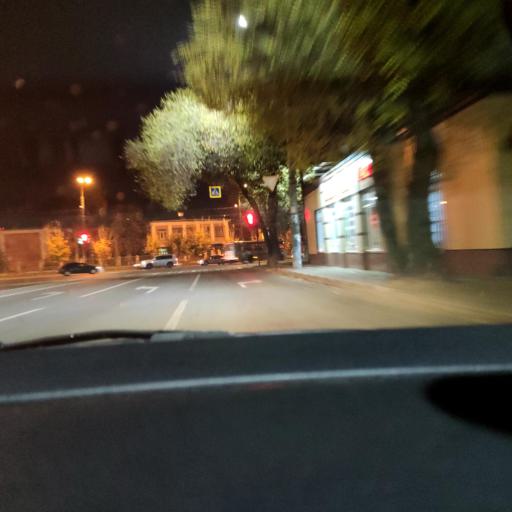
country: RU
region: Voronezj
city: Voronezh
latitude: 51.6711
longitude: 39.1618
